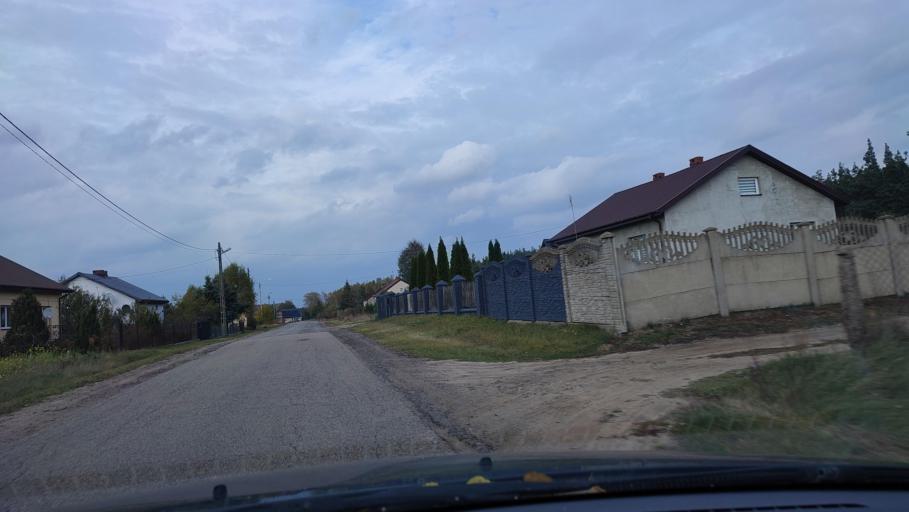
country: PL
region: Masovian Voivodeship
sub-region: Powiat mlawski
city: Mlawa
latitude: 53.1657
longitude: 20.3637
